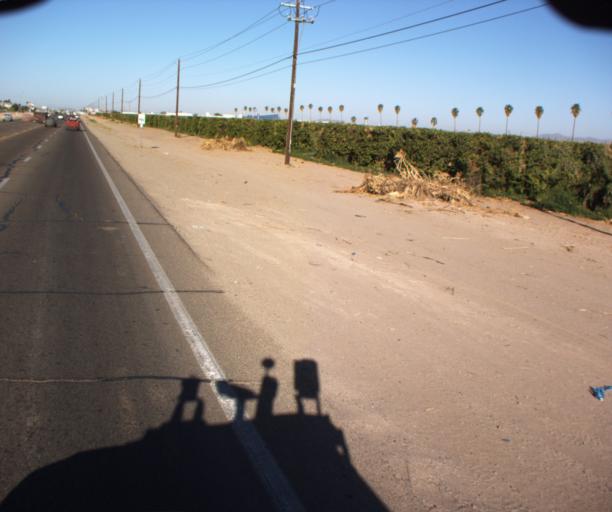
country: US
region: Arizona
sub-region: Yuma County
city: Yuma
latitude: 32.6699
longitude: -114.5647
